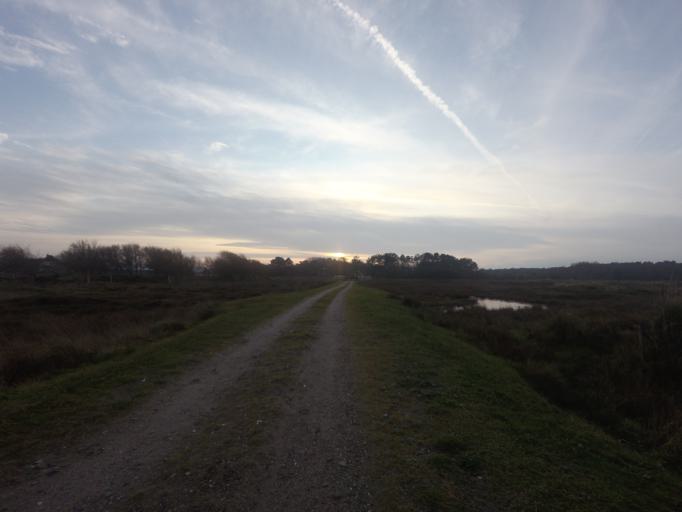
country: NL
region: North Holland
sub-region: Gemeente Texel
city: Den Burg
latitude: 53.1052
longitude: 4.7741
